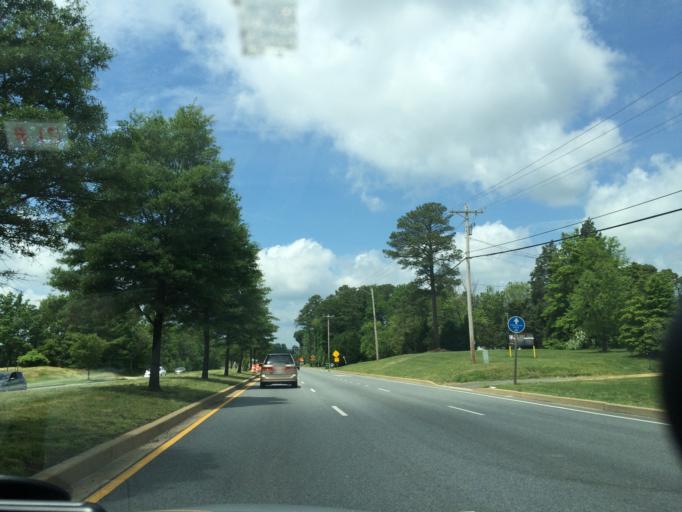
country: US
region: Maryland
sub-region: Saint Mary's County
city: California
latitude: 38.3046
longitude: -76.5219
